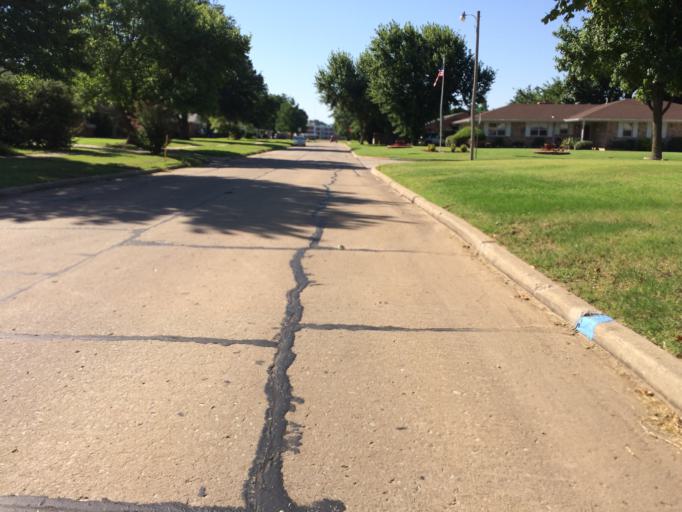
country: US
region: Oklahoma
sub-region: Cleveland County
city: Norman
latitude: 35.2298
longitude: -97.4629
